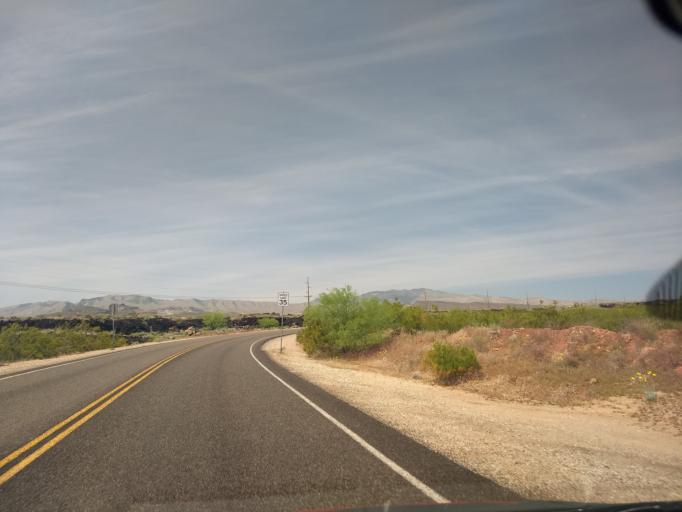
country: US
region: Utah
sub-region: Washington County
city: Santa Clara
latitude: 37.1418
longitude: -113.6407
